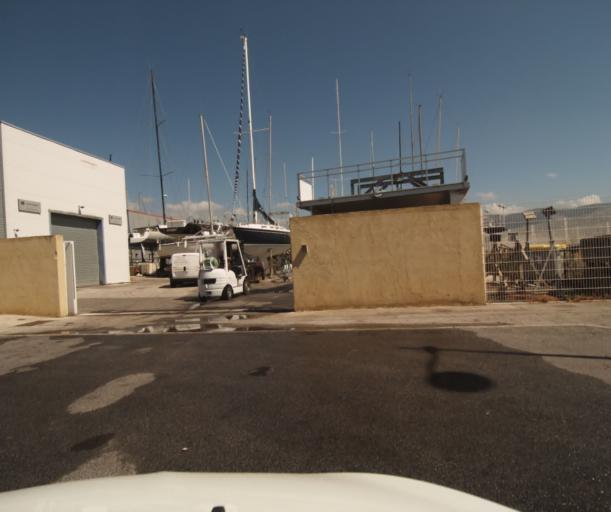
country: FR
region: Provence-Alpes-Cote d'Azur
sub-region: Departement du Var
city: La Seyne-sur-Mer
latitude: 43.1036
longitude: 5.9021
